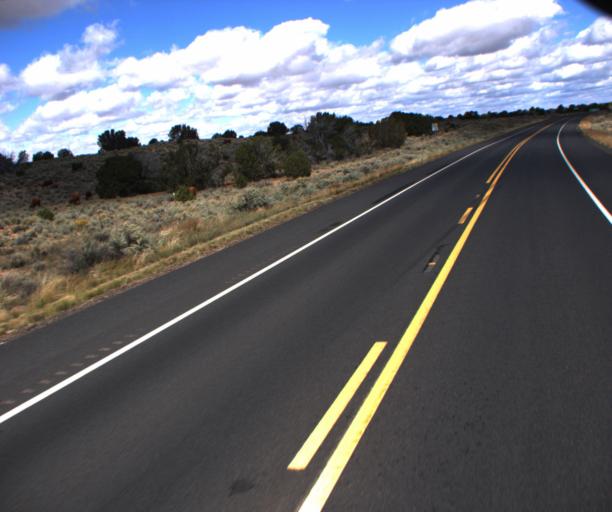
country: US
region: Arizona
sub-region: Apache County
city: Houck
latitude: 35.1674
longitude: -109.3380
